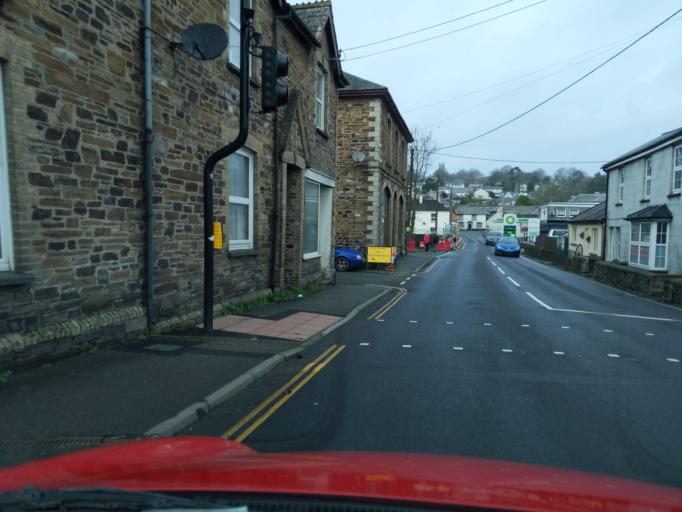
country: GB
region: England
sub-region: Cornwall
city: Launceston
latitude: 50.6410
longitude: -4.3646
